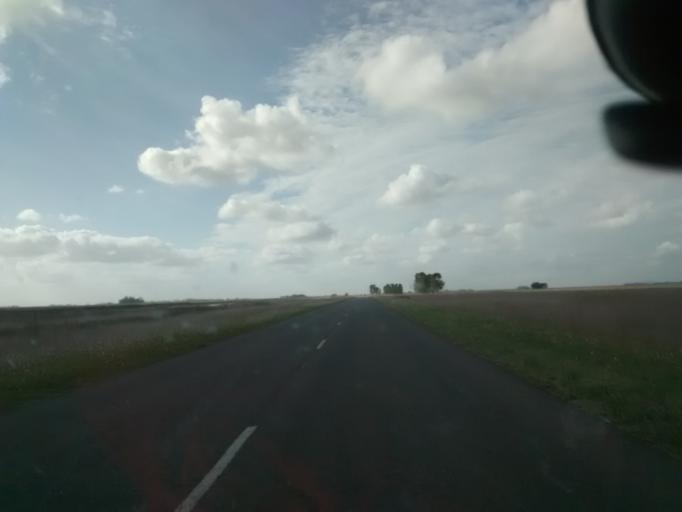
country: AR
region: Buenos Aires
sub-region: Partido de Ayacucho
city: Ayacucho
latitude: -37.3153
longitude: -58.4691
